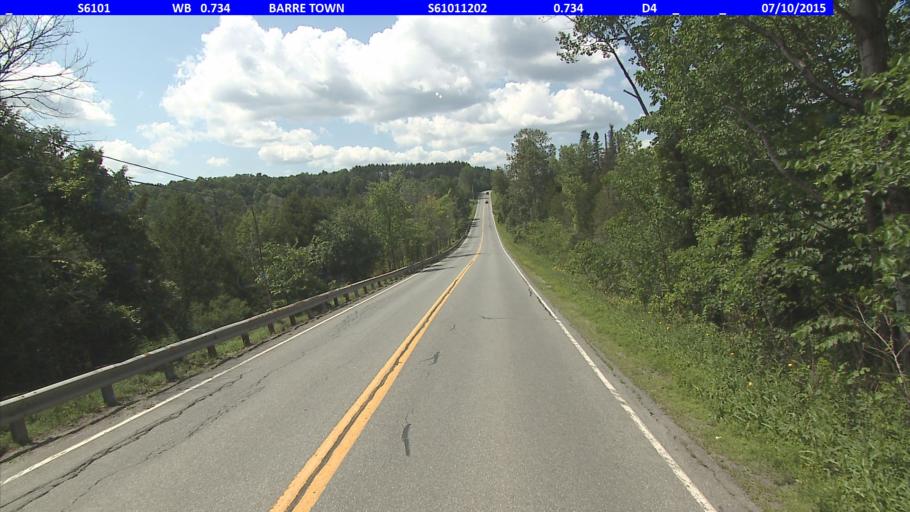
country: US
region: Vermont
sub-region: Washington County
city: South Barre
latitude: 44.1864
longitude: -72.5324
